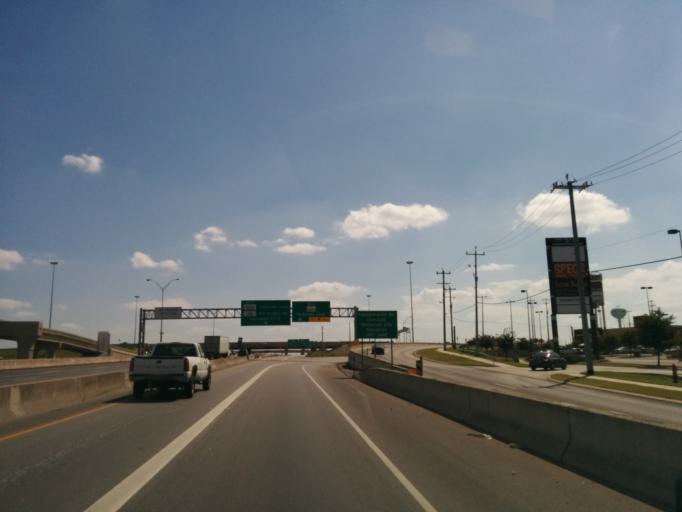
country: US
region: Texas
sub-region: Bexar County
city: Live Oak
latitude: 29.5705
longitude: -98.3306
